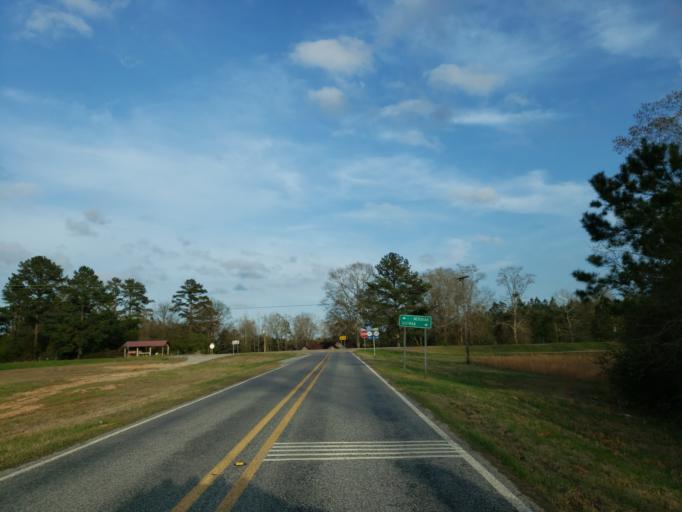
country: US
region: Mississippi
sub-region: Clarke County
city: Stonewall
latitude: 32.1734
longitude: -88.6802
